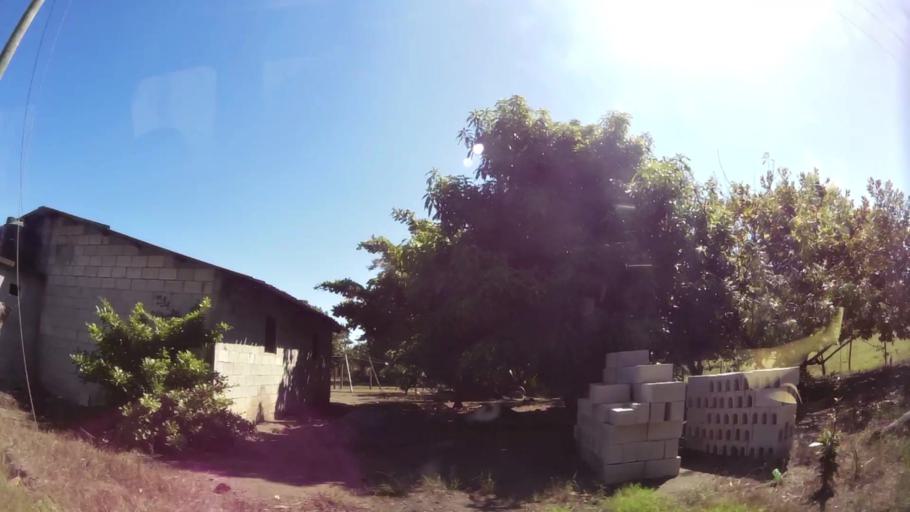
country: GT
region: Escuintla
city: Iztapa
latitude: 13.9228
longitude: -90.5997
